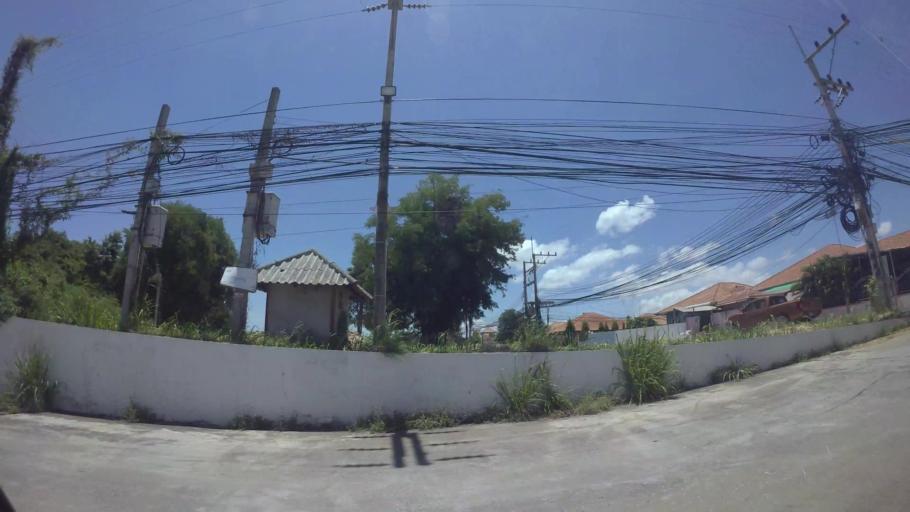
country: TH
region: Chon Buri
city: Phatthaya
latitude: 12.9203
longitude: 100.9023
